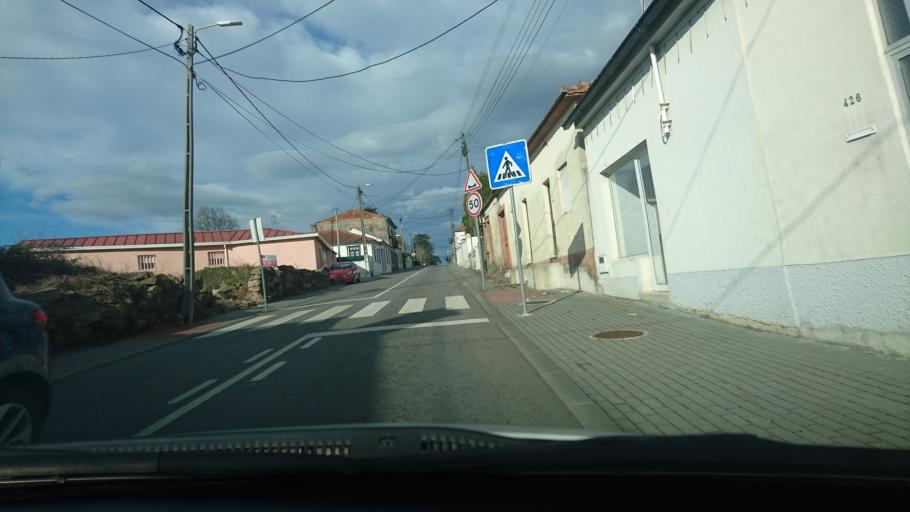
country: PT
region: Aveiro
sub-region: Santa Maria da Feira
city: Pacos de Brandao
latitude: 40.9680
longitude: -8.5914
